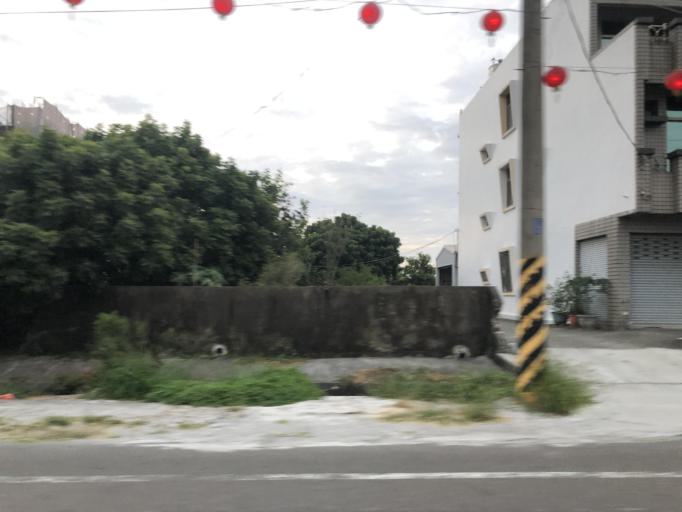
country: TW
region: Taiwan
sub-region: Tainan
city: Tainan
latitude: 23.0275
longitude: 120.2929
